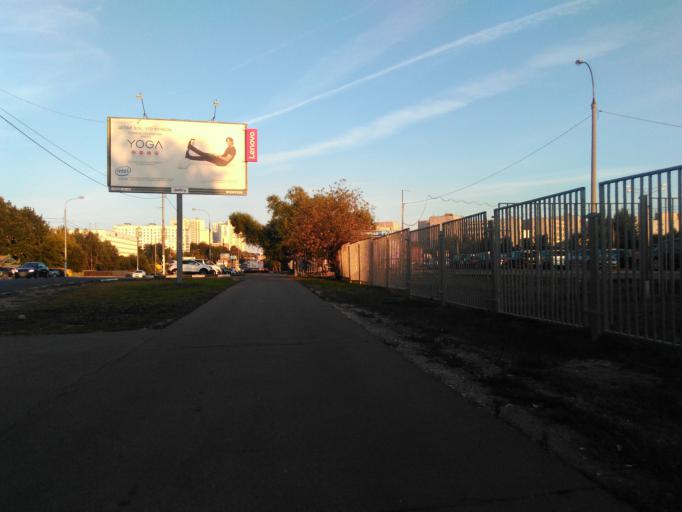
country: RU
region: Moscow
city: Troparevo
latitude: 55.6509
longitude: 37.5064
